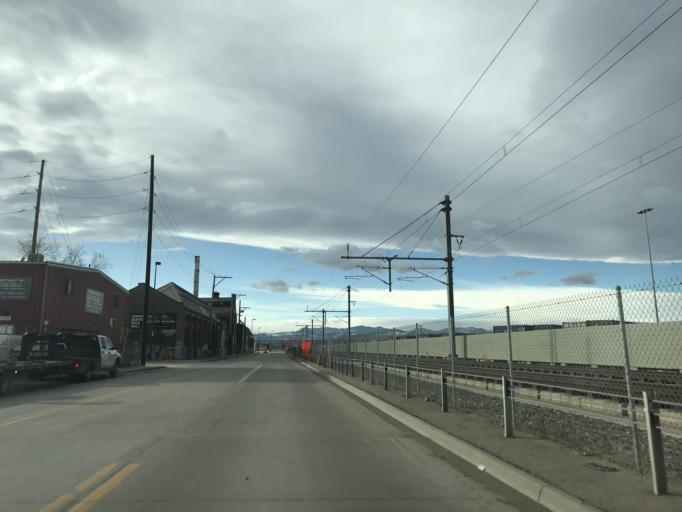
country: US
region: Colorado
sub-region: Denver County
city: Denver
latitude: 39.7728
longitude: -104.9652
